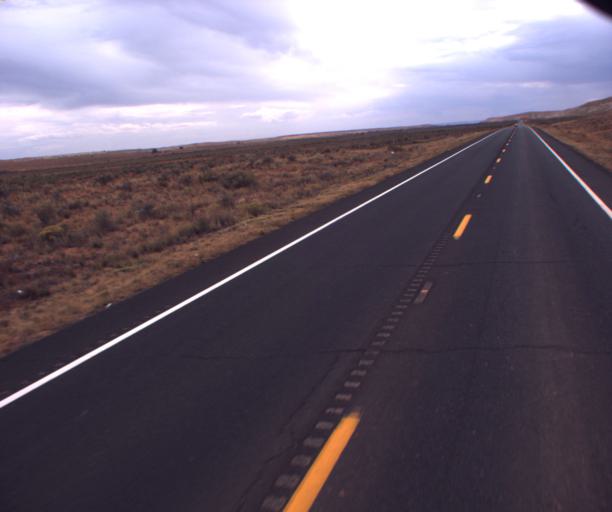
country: US
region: Arizona
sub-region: Coconino County
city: Kaibito
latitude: 36.3485
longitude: -110.9117
